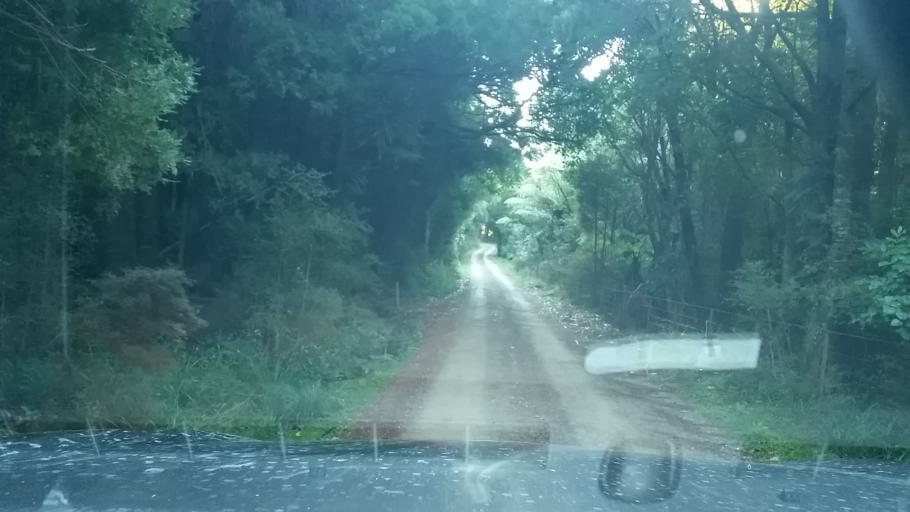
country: NZ
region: Marlborough
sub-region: Marlborough District
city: Picton
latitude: -41.0570
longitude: 174.1100
